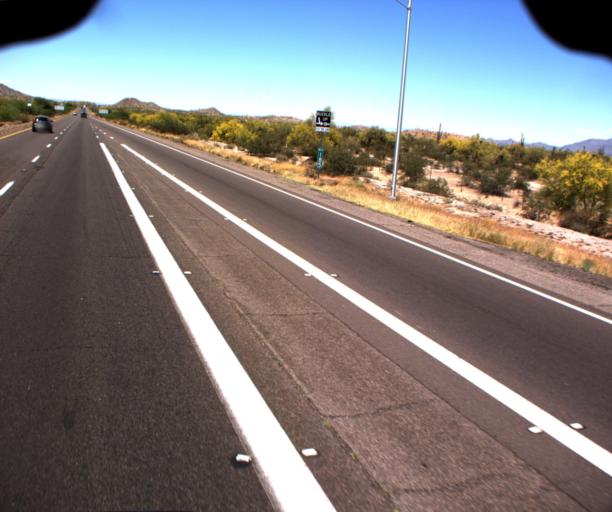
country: US
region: Arizona
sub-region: Pinal County
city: Sacaton
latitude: 33.0067
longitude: -111.7557
